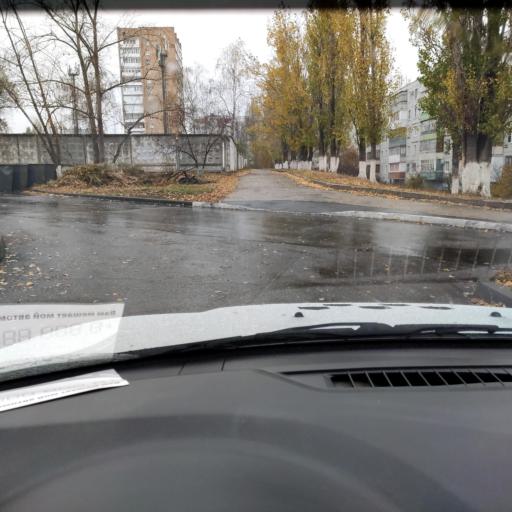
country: RU
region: Samara
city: Zhigulevsk
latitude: 53.4788
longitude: 49.4551
